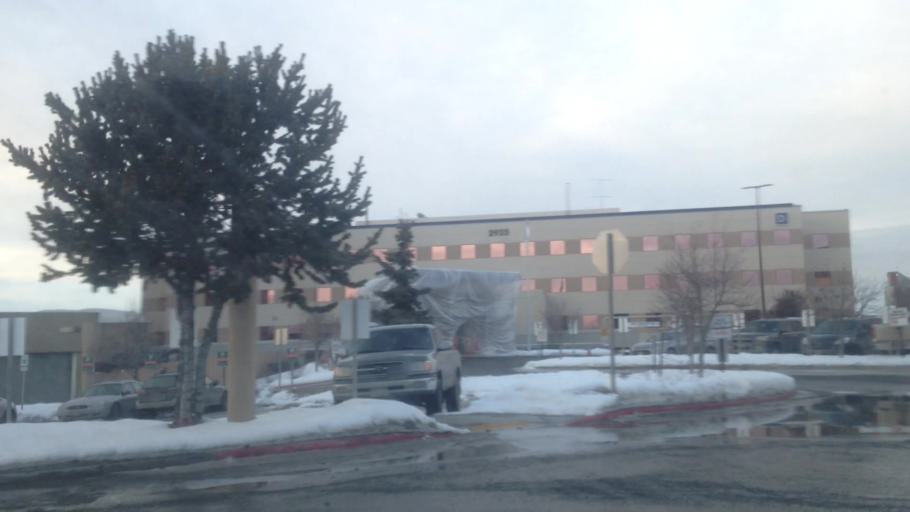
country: US
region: Alaska
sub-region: Anchorage Municipality
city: Anchorage
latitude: 61.2102
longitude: -149.8270
